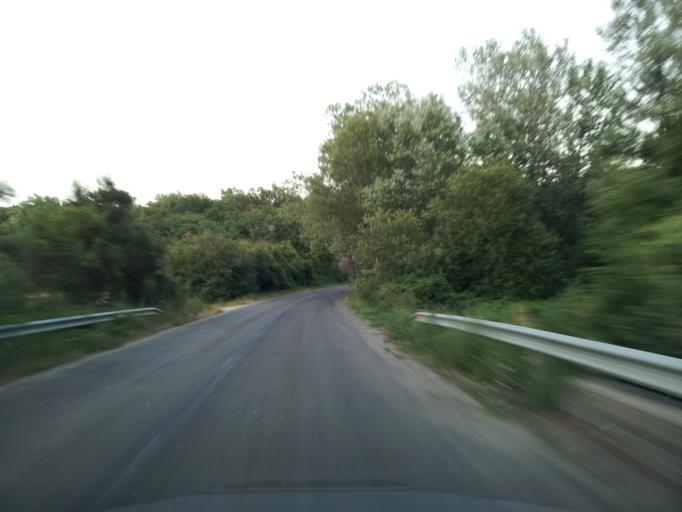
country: HU
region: Fejer
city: Szarliget
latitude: 47.5250
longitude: 18.4927
